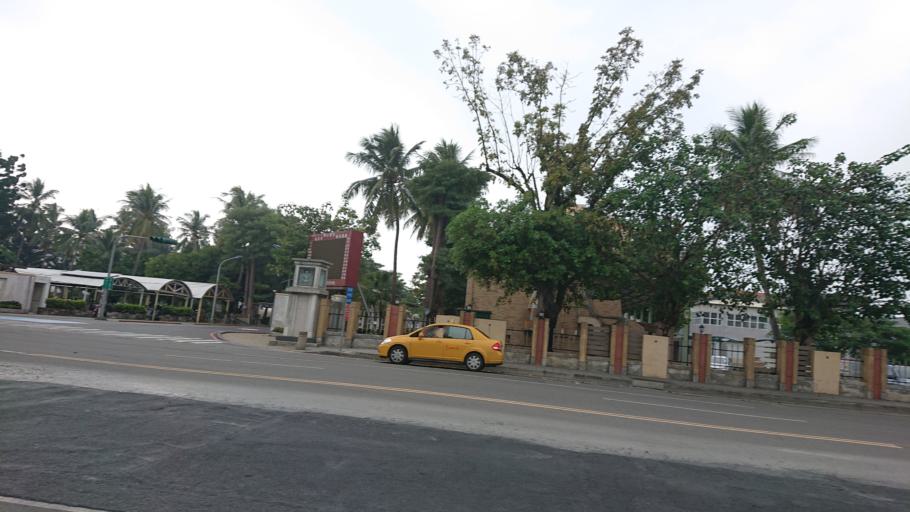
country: TW
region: Kaohsiung
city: Kaohsiung
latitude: 22.7016
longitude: 120.2926
